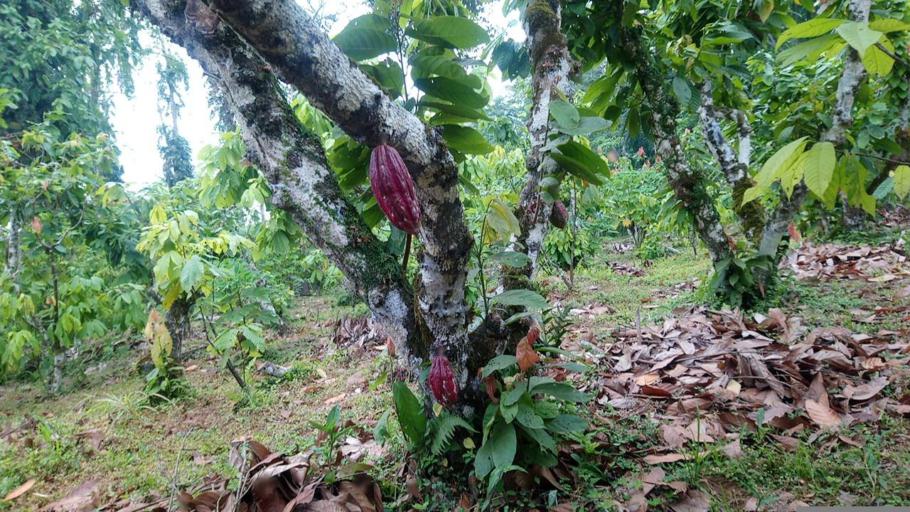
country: BO
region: La Paz
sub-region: Provincia Larecaja
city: Guanay
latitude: -15.5631
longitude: -67.3220
